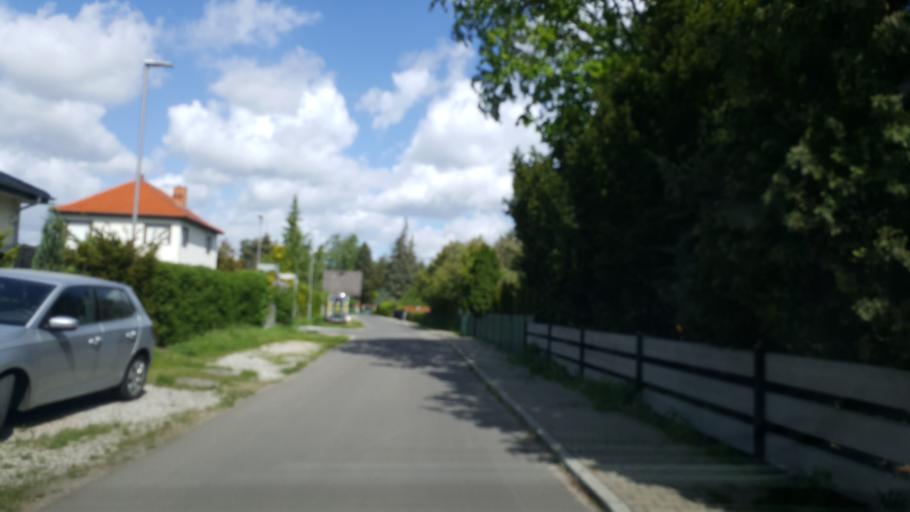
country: DE
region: Berlin
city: Bohnsdorf
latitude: 52.3976
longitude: 13.5856
